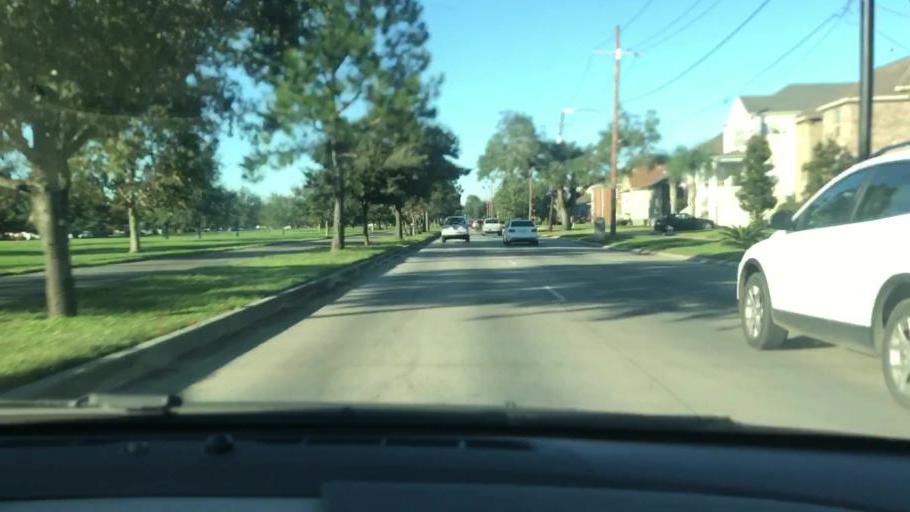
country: US
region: Louisiana
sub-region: Jefferson Parish
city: Metairie
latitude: 30.0016
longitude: -90.1149
